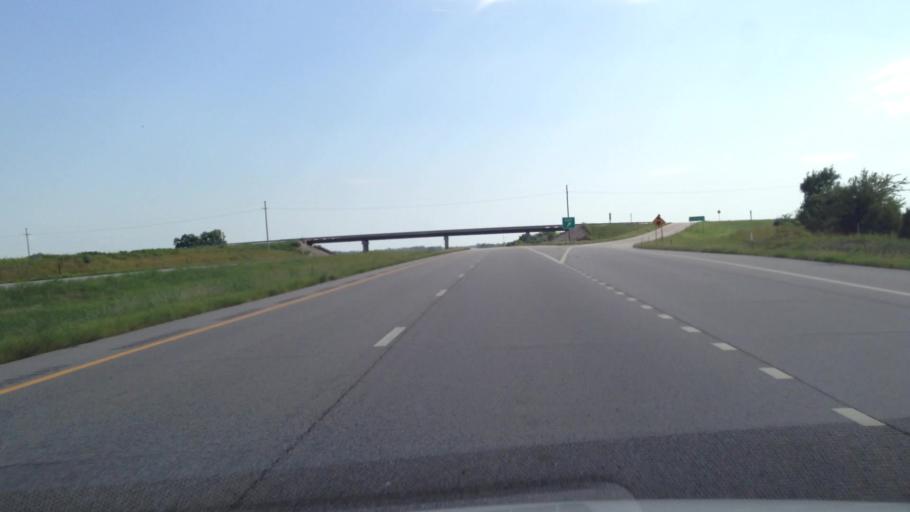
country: US
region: Kansas
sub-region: Linn County
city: La Cygne
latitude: 38.4062
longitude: -94.6881
